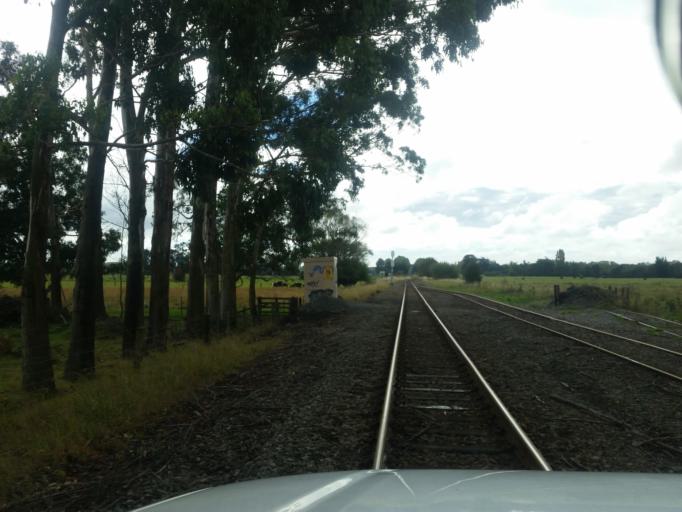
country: NZ
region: Canterbury
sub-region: Waimakariri District
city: Kaiapoi
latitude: -43.4437
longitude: 172.6413
